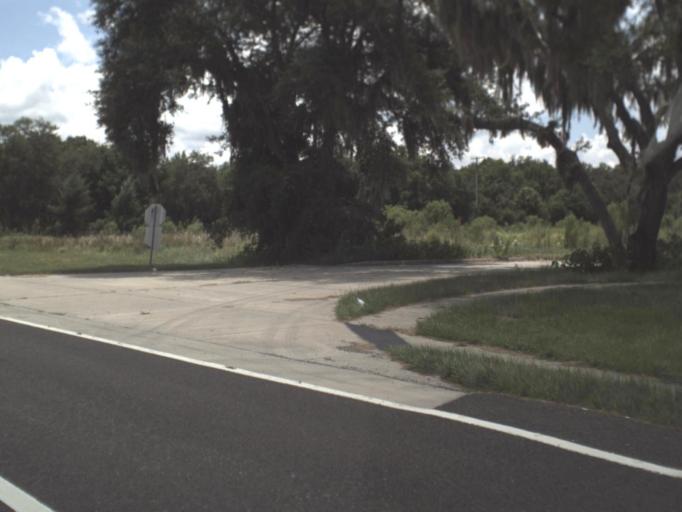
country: US
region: Florida
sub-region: Hillsborough County
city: Ruskin
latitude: 27.7129
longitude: -82.4158
